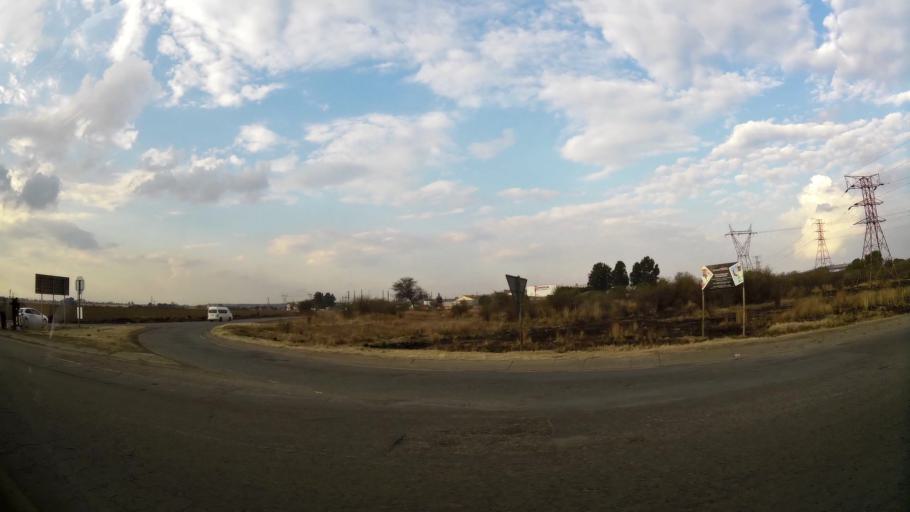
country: ZA
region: Gauteng
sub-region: Sedibeng District Municipality
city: Vanderbijlpark
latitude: -26.6735
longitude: 27.7909
